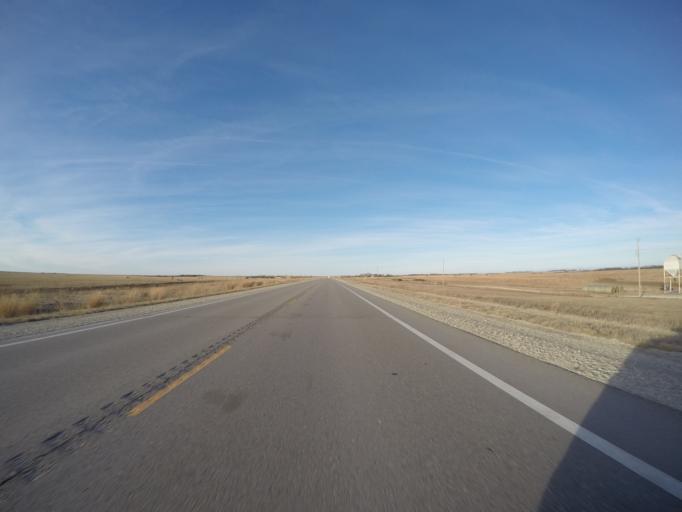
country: US
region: Kansas
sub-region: Marion County
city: Marion
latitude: 38.3371
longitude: -96.9667
